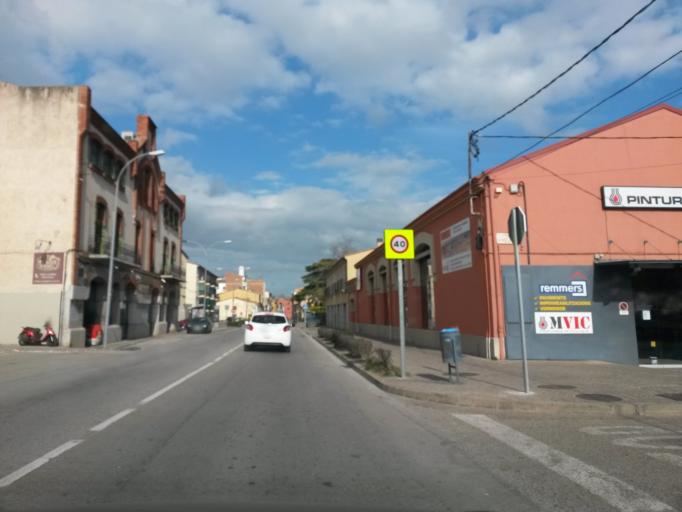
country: ES
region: Catalonia
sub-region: Provincia de Girona
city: Sarria de Ter
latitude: 42.0093
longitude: 2.8251
